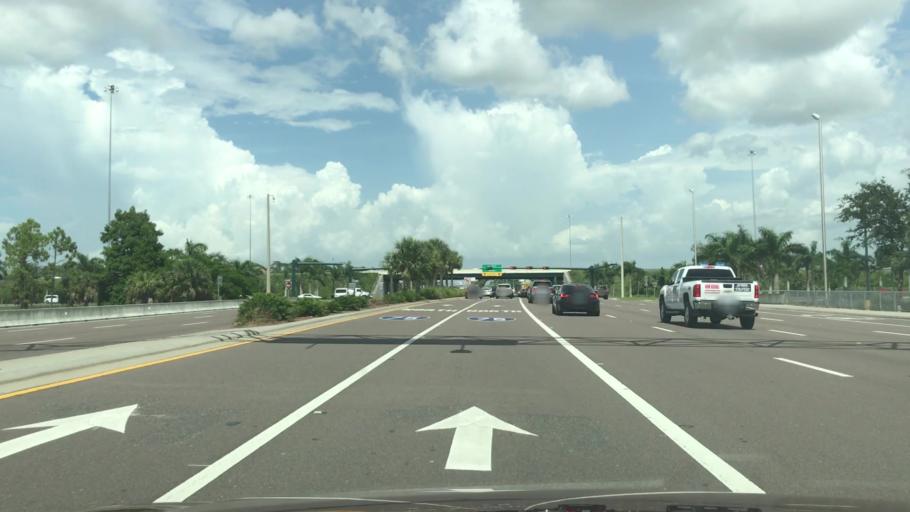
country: US
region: Florida
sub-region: Collier County
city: Vineyards
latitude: 26.2728
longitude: -81.7453
